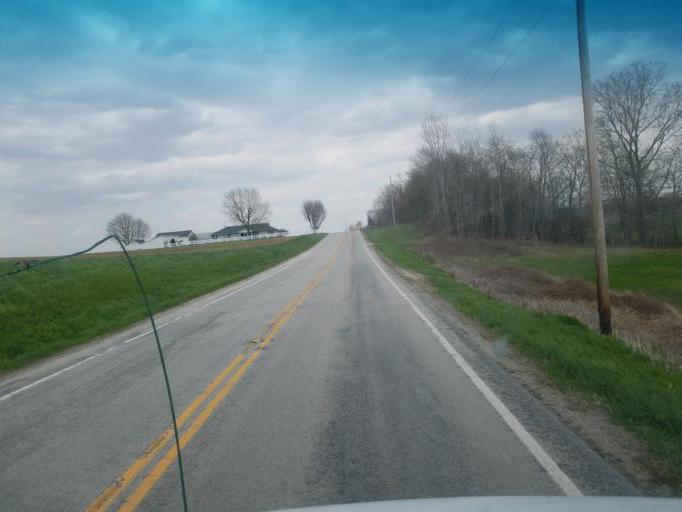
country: US
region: Ohio
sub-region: Seneca County
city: Tiffin
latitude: 40.9499
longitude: -83.1395
